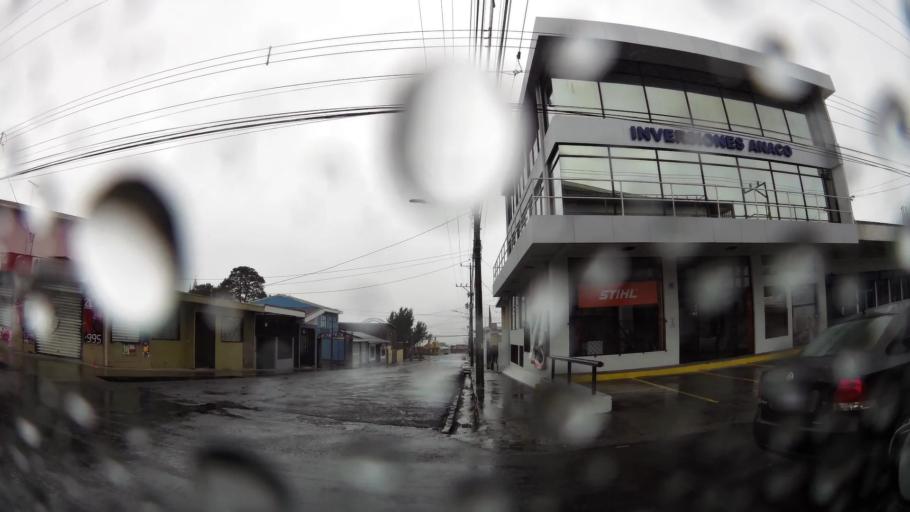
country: CR
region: Cartago
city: Cartago
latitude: 9.8665
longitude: -83.9276
